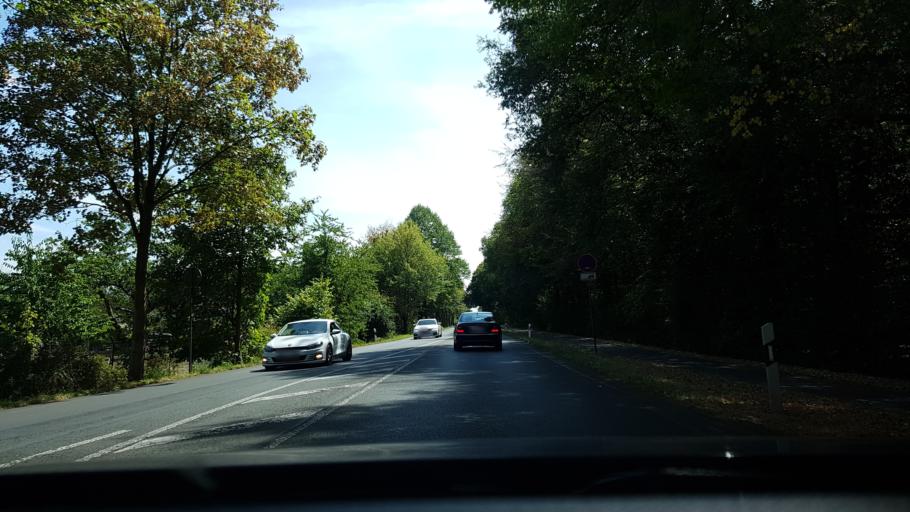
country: DE
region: North Rhine-Westphalia
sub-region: Regierungsbezirk Dusseldorf
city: Voerde
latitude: 51.5962
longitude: 6.7104
